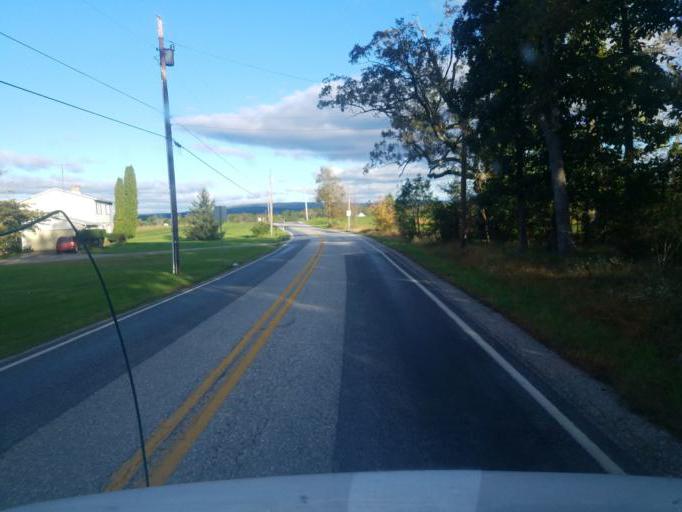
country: US
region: Pennsylvania
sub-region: Adams County
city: Biglerville
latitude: 39.9066
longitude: -77.2165
